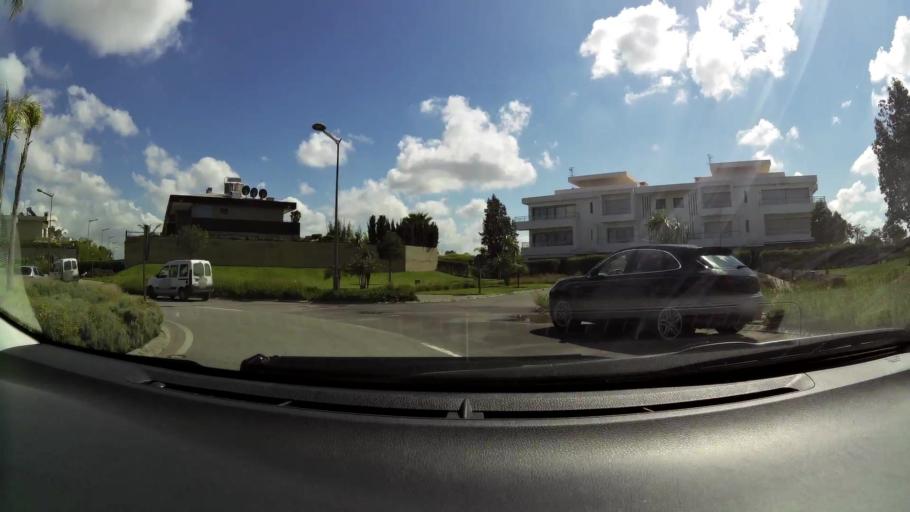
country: MA
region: Grand Casablanca
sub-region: Nouaceur
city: Bouskoura
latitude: 33.4709
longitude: -7.6102
